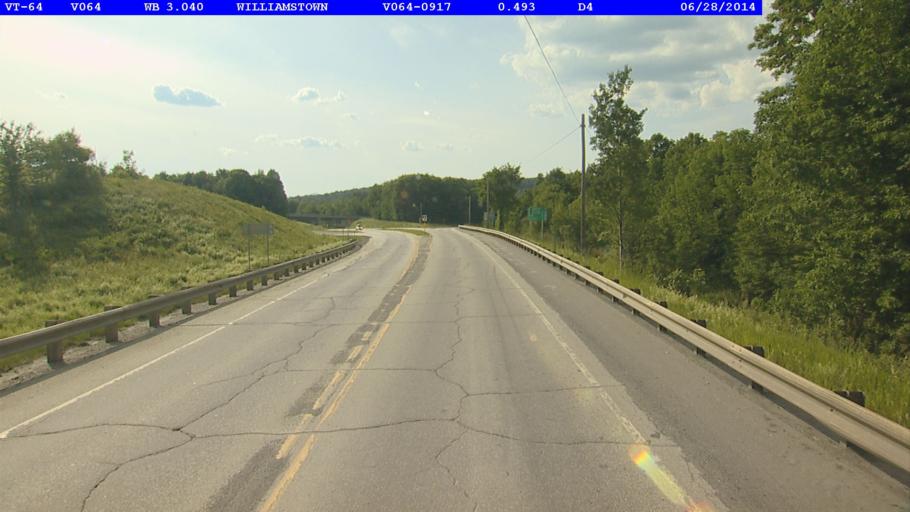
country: US
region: Vermont
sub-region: Orange County
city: Williamstown
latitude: 44.1138
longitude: -72.6039
